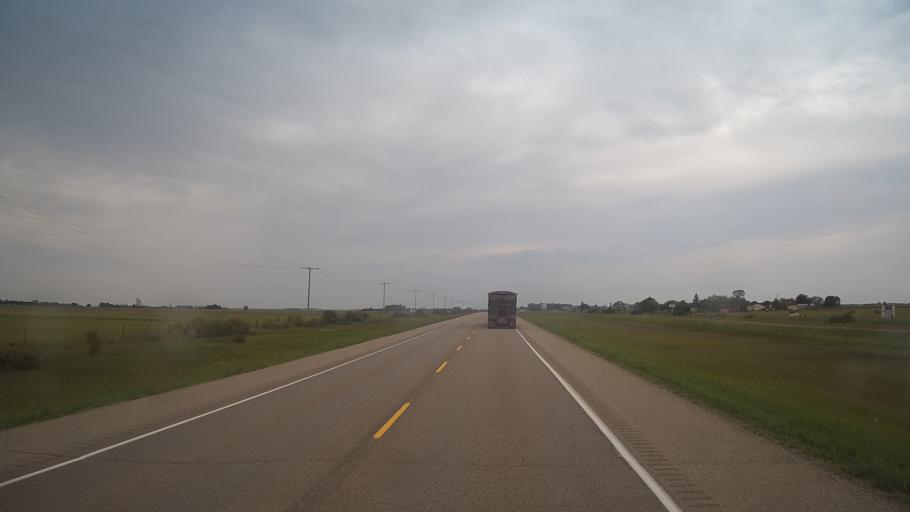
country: CA
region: Saskatchewan
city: Langham
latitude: 52.1289
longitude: -107.1860
